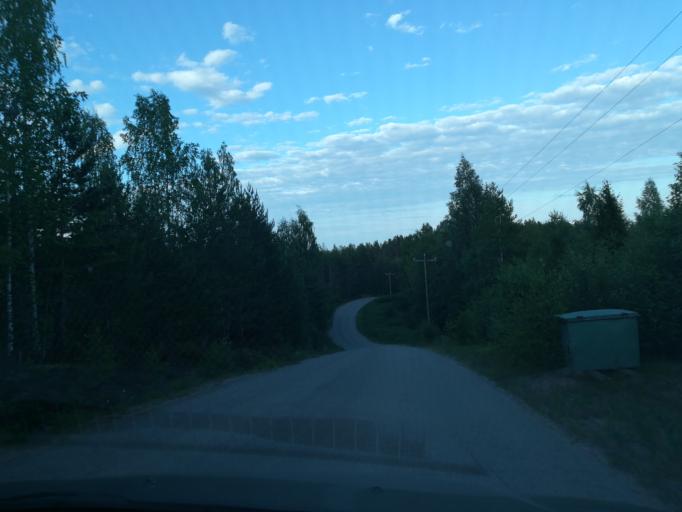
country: FI
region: Southern Savonia
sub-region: Mikkeli
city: Puumala
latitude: 61.5807
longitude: 28.1267
